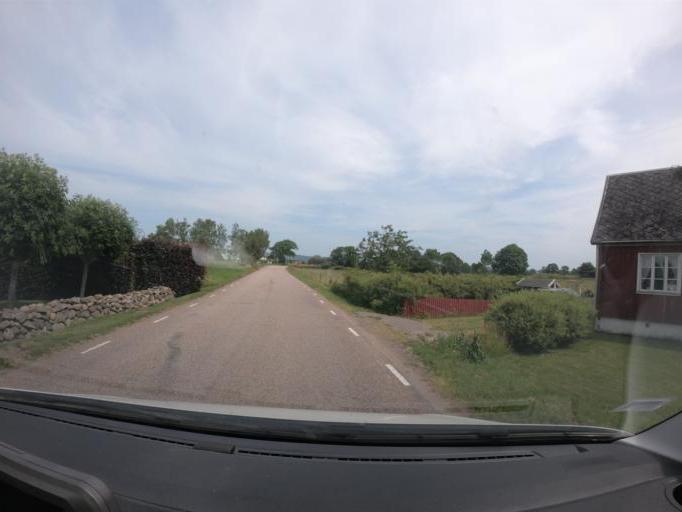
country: SE
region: Skane
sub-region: Angelholms Kommun
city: Vejbystrand
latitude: 56.3143
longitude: 12.7999
